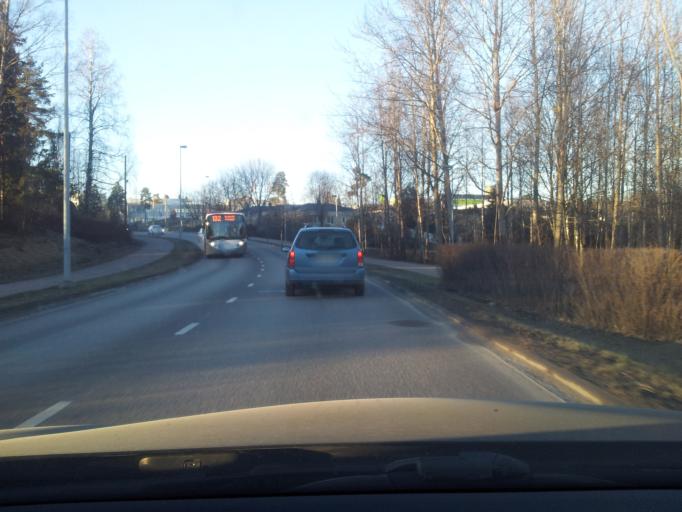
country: FI
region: Uusimaa
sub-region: Helsinki
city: Koukkuniemi
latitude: 60.1592
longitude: 24.7258
